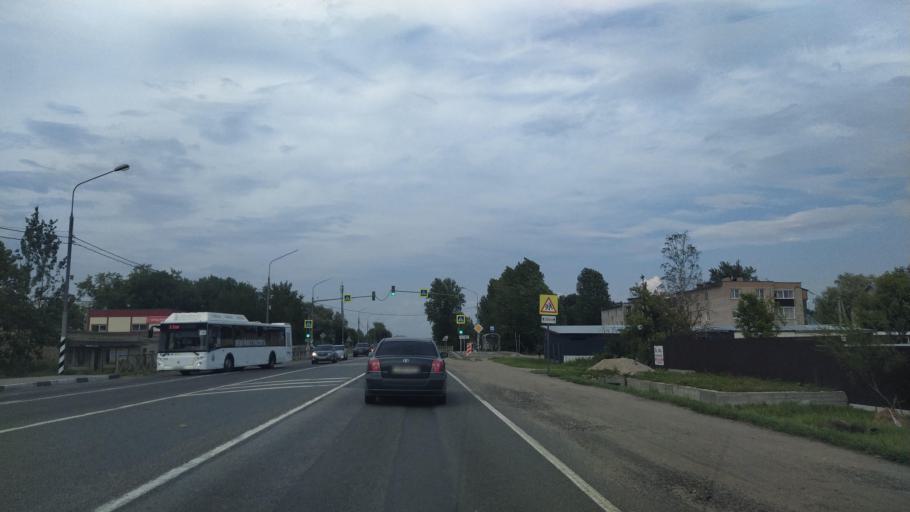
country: RU
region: Novgorod
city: Pankovka
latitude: 58.4896
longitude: 31.2005
